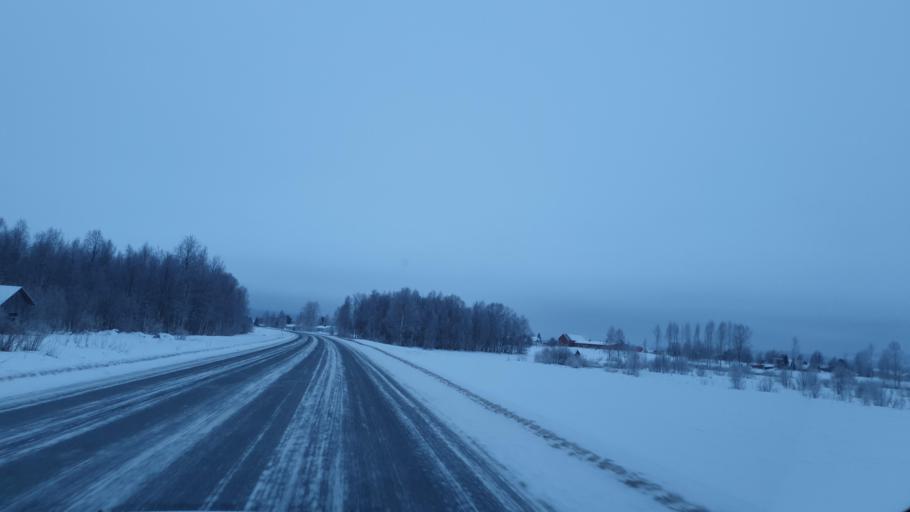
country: SE
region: Norrbotten
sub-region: Overtornea Kommun
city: OEvertornea
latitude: 66.4324
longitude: 23.6667
